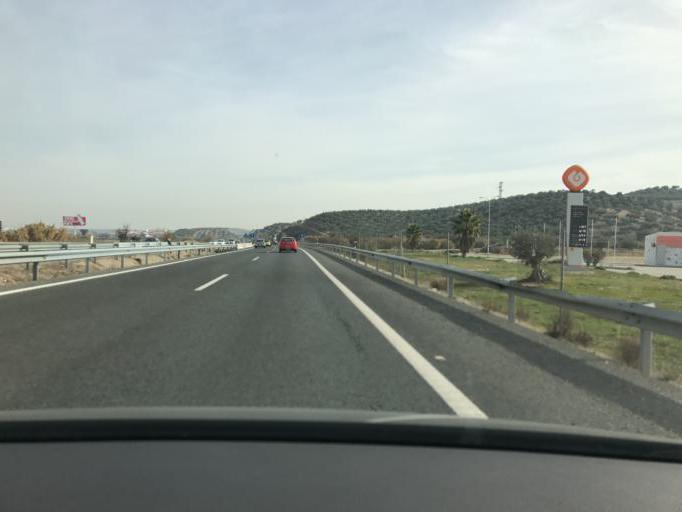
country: ES
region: Andalusia
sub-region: Provincia de Granada
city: Huetor-Tajar
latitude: 37.1803
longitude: -4.0600
